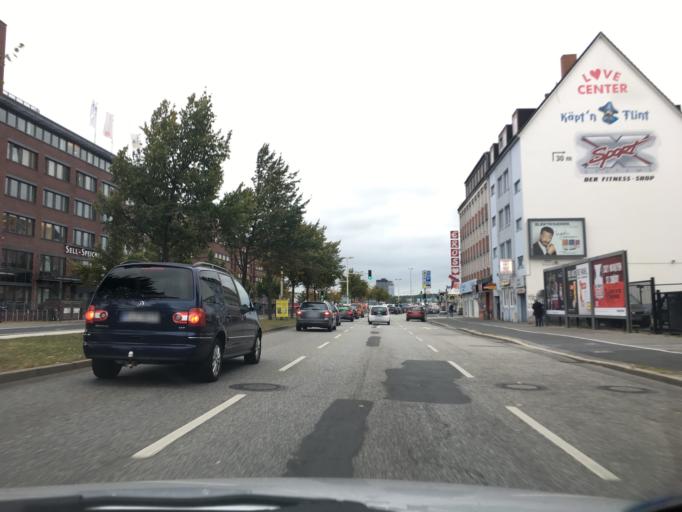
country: DE
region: Schleswig-Holstein
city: Kiel
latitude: 54.3230
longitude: 10.1431
